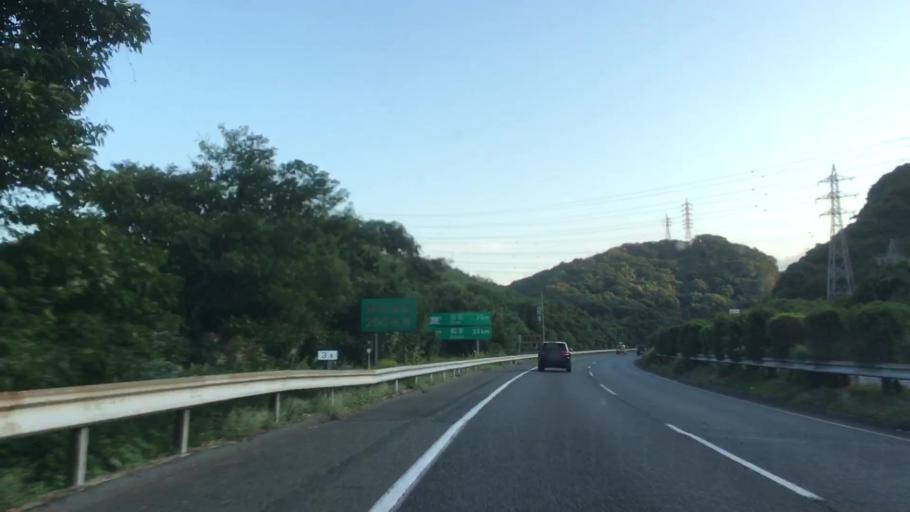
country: JP
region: Yamaguchi
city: Shimonoseki
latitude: 33.8966
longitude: 130.9724
